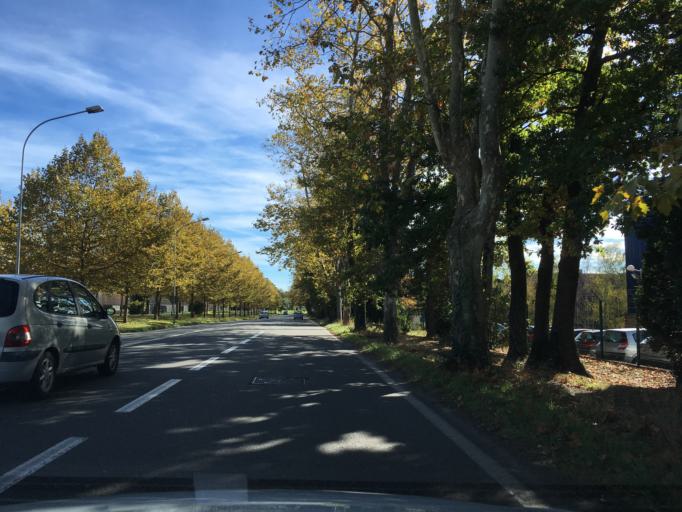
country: FR
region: Aquitaine
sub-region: Departement des Pyrenees-Atlantiques
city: Buros
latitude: 43.3211
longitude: -0.3116
